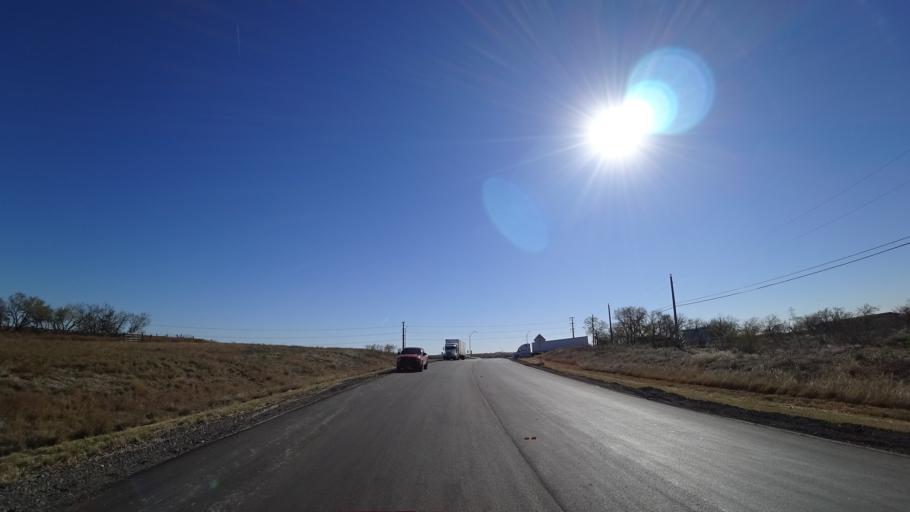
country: US
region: Texas
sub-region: Travis County
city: Onion Creek
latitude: 30.1191
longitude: -97.6621
